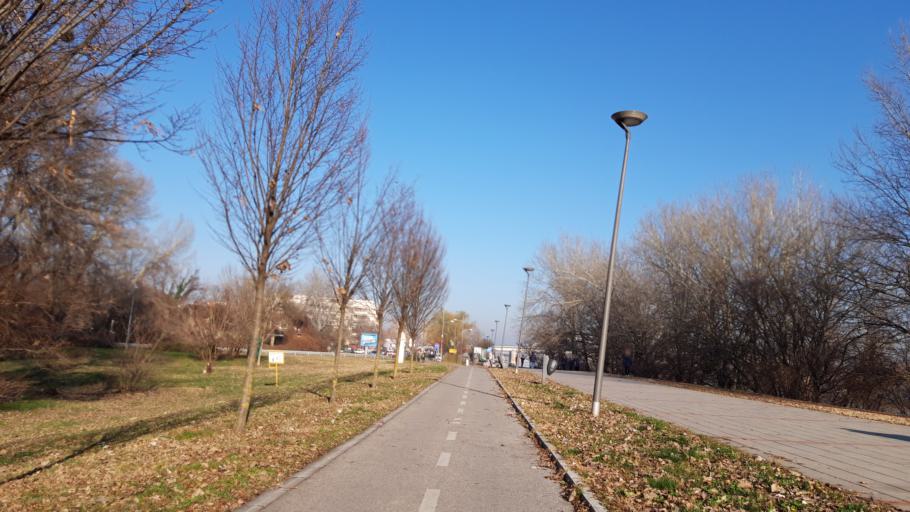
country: RS
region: Autonomna Pokrajina Vojvodina
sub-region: Juznobacki Okrug
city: Novi Sad
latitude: 45.2488
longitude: 19.8558
